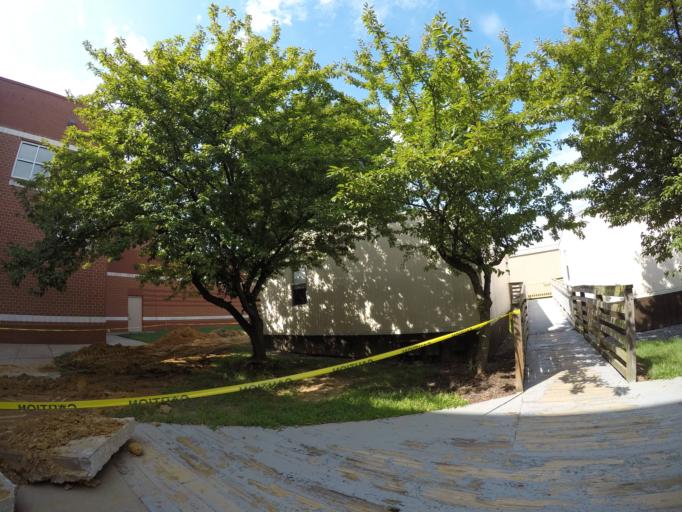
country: US
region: Maryland
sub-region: Howard County
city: Ellicott City
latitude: 39.2501
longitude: -76.8101
